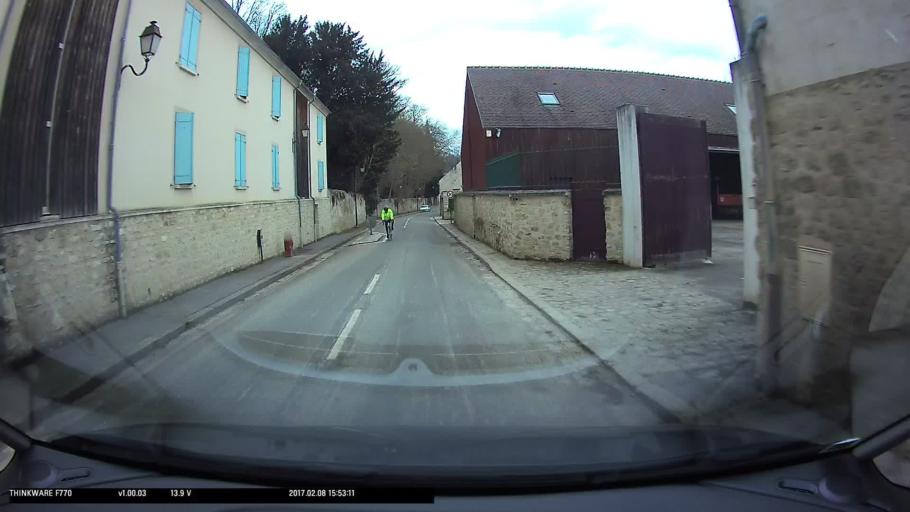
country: FR
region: Ile-de-France
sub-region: Departement du Val-d'Oise
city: Vigny
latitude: 49.0744
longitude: 1.9261
